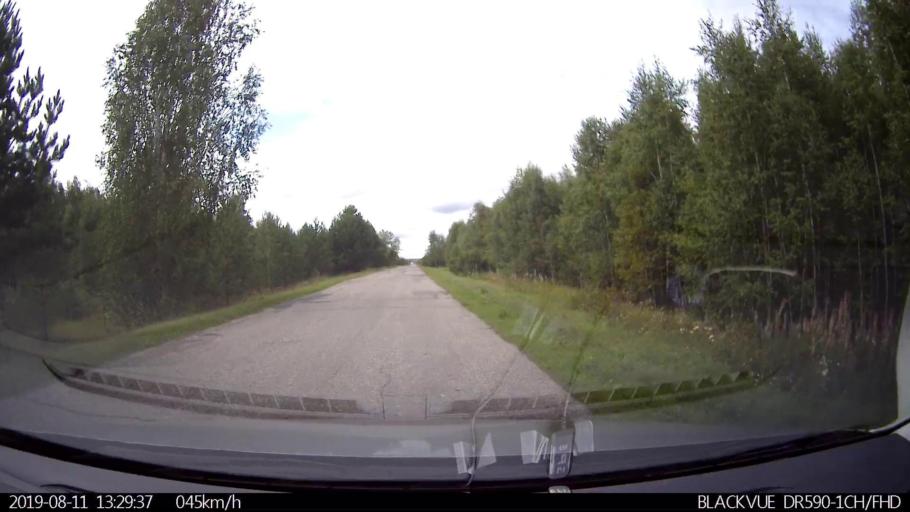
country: RU
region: Ulyanovsk
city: Ignatovka
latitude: 53.8598
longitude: 47.6126
